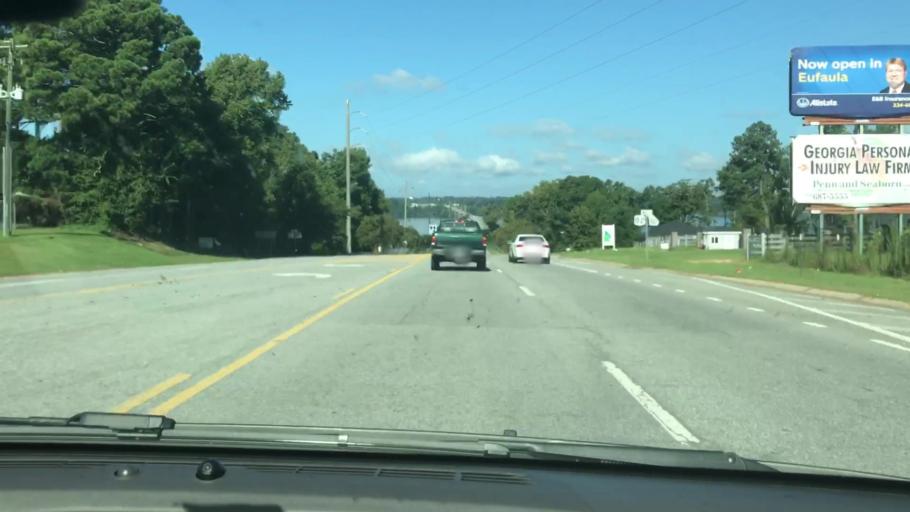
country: US
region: Georgia
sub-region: Quitman County
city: Georgetown
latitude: 31.8882
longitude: -85.1103
